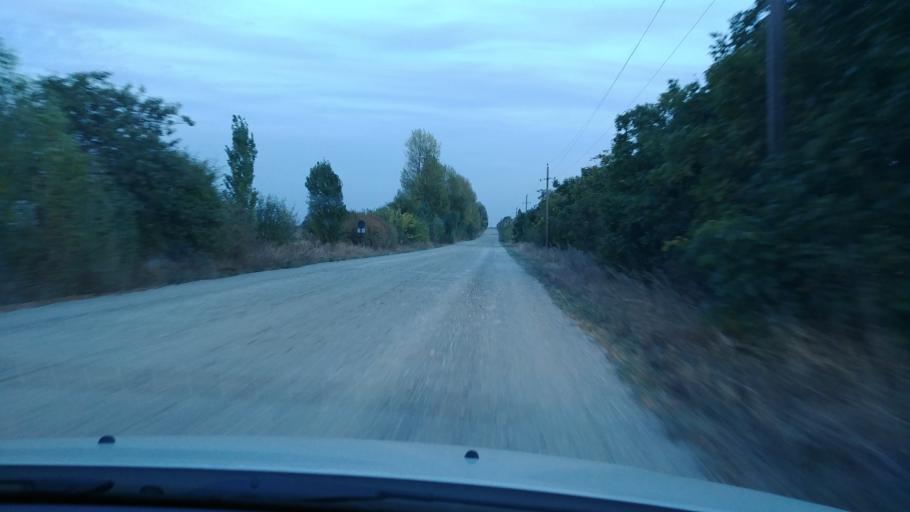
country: MD
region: Rezina
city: Saharna
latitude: 47.6733
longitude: 28.9366
